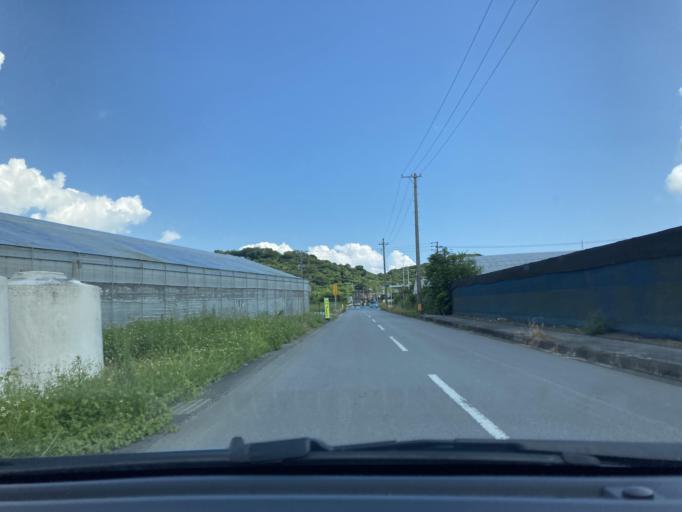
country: JP
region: Okinawa
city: Tomigusuku
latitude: 26.1598
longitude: 127.7553
